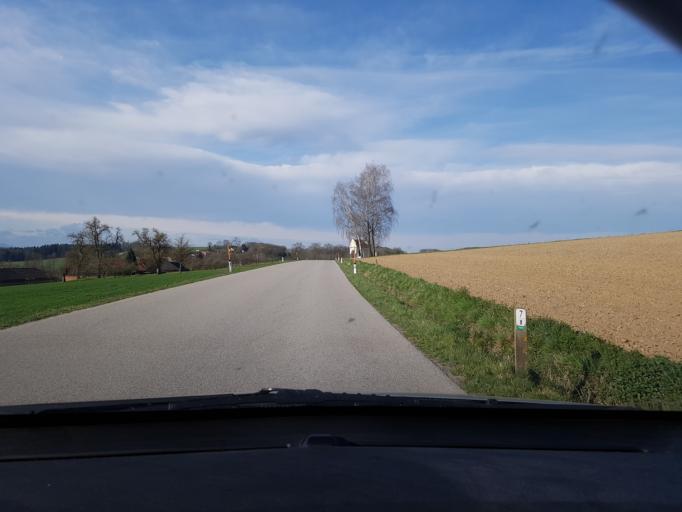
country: AT
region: Upper Austria
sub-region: Politischer Bezirk Linz-Land
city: Sankt Florian
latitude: 48.1588
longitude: 14.3948
